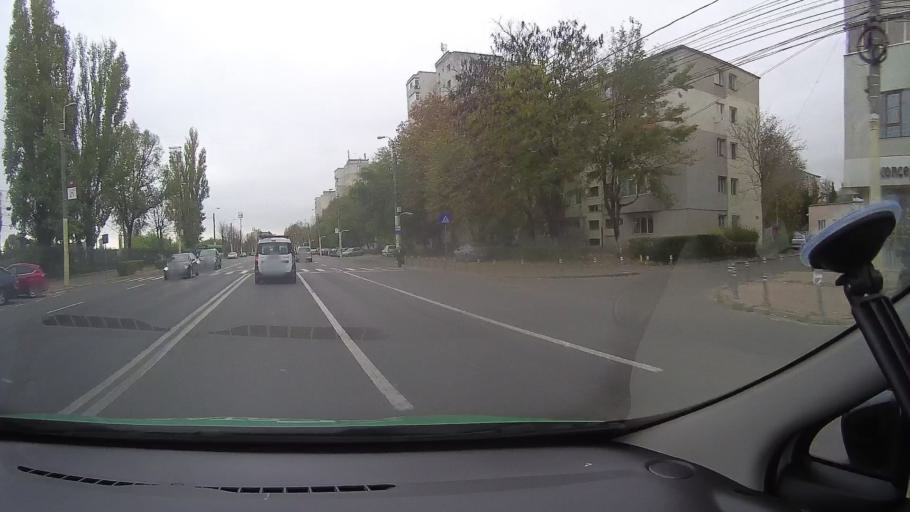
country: RO
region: Constanta
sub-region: Municipiul Constanta
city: Constanta
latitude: 44.1716
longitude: 28.6215
